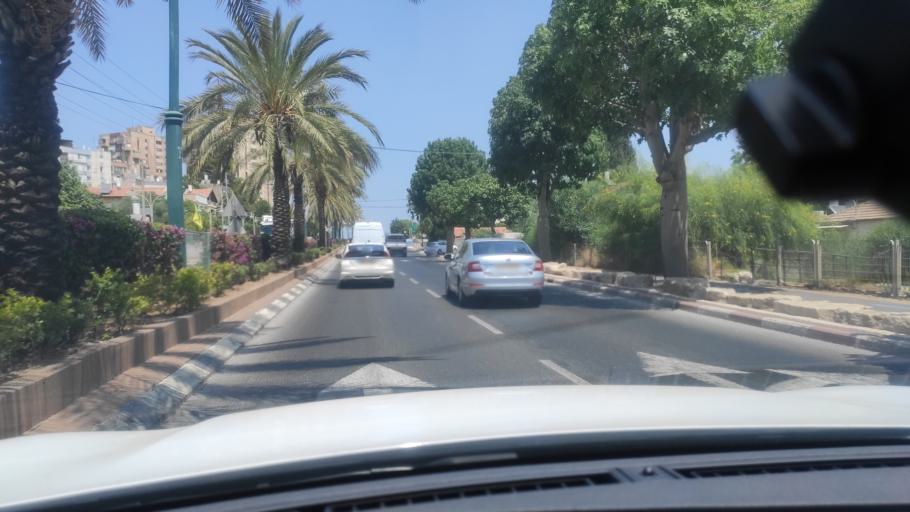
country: IL
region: Central District
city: Petah Tiqwa
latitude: 32.0981
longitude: 34.9008
